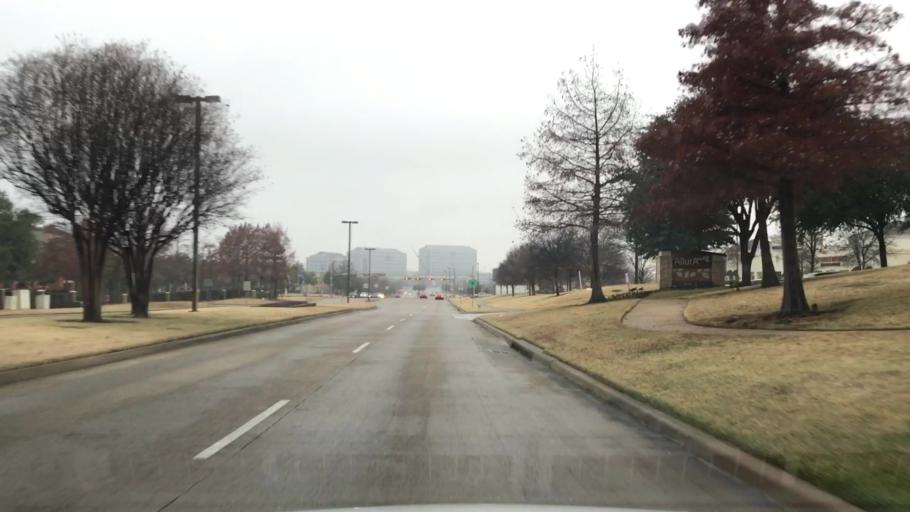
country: US
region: Texas
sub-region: Dallas County
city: Farmers Branch
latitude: 32.8960
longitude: -96.9562
